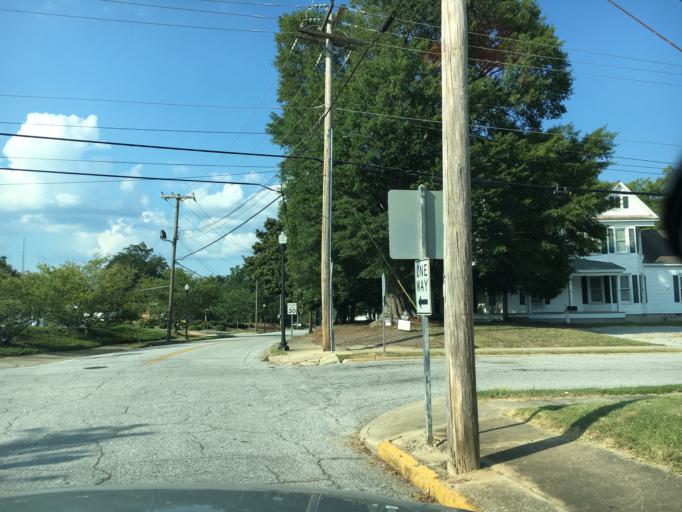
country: US
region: South Carolina
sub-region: Laurens County
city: Clinton
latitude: 34.4750
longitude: -81.8799
